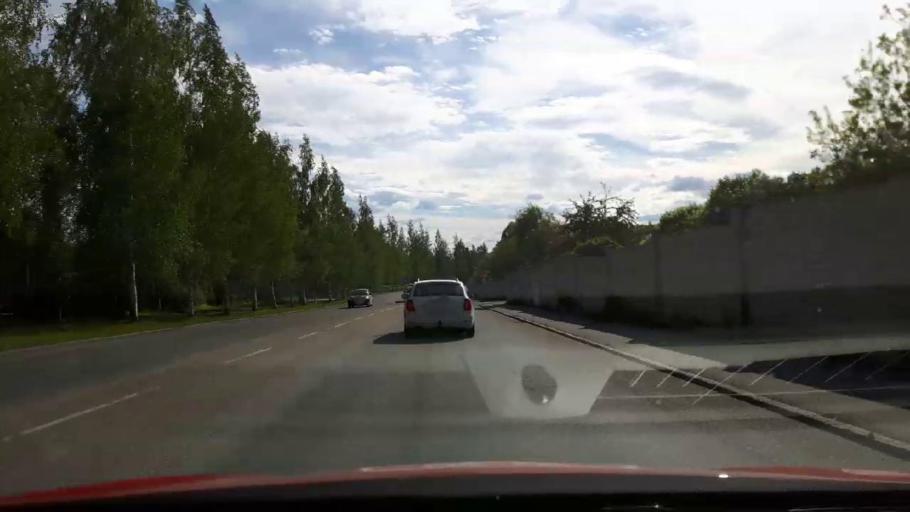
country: SE
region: Jaemtland
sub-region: OEstersunds Kommun
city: Ostersund
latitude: 63.1782
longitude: 14.6552
